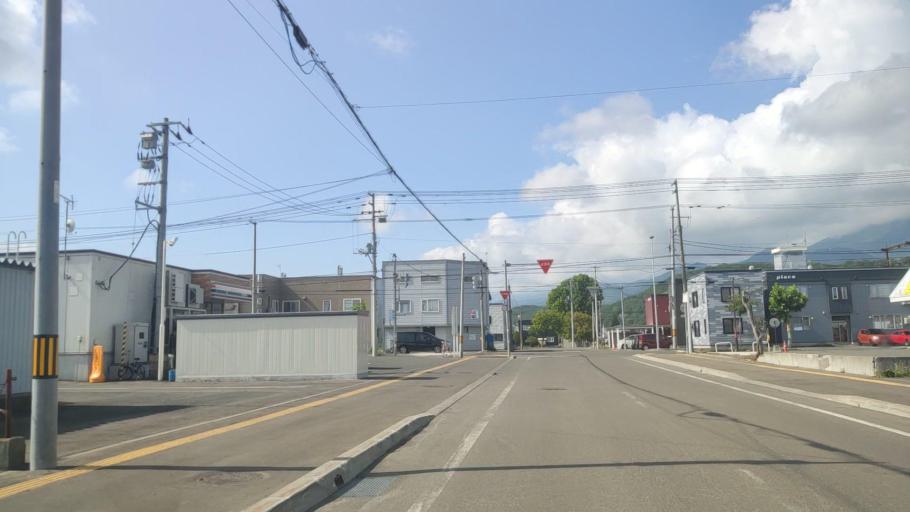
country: JP
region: Hokkaido
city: Shimo-furano
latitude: 43.3431
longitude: 142.3853
